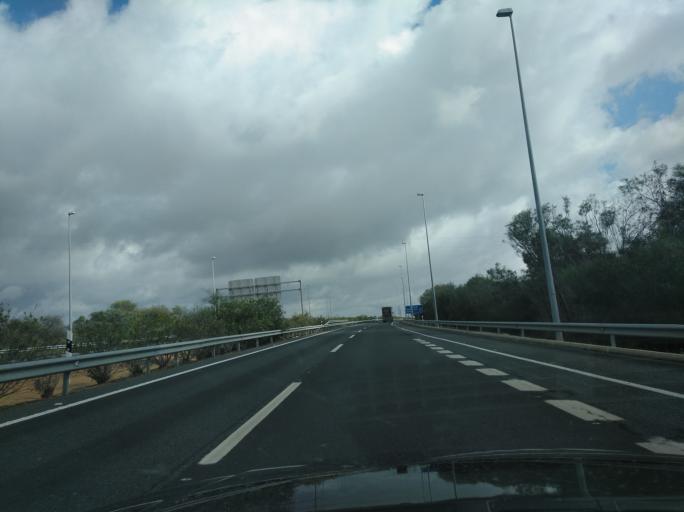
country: ES
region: Andalusia
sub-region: Provincia de Huelva
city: Lepe
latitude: 37.3005
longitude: -7.2143
